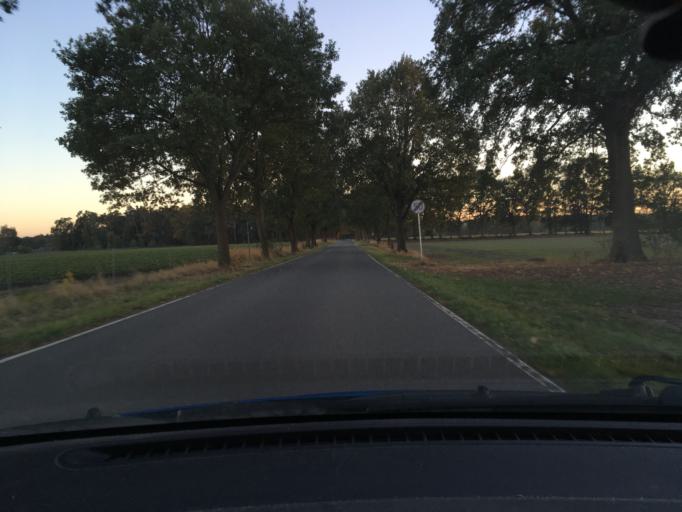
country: DE
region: Lower Saxony
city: Neetze
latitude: 53.3026
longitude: 10.6164
